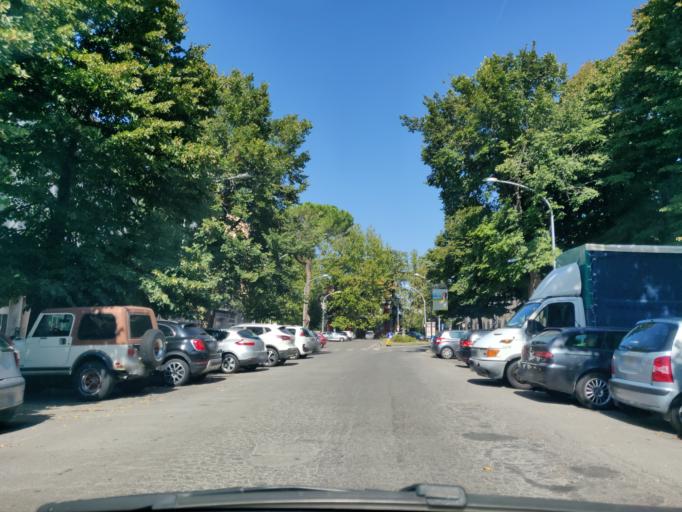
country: IT
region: Latium
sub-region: Provincia di Viterbo
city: Viterbo
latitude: 42.4244
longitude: 12.1062
